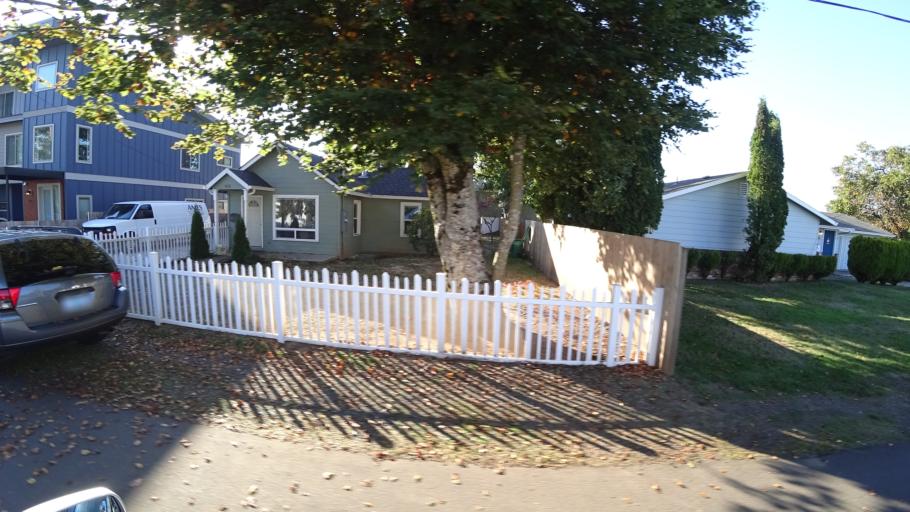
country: US
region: Oregon
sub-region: Multnomah County
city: Gresham
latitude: 45.5037
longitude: -122.4339
